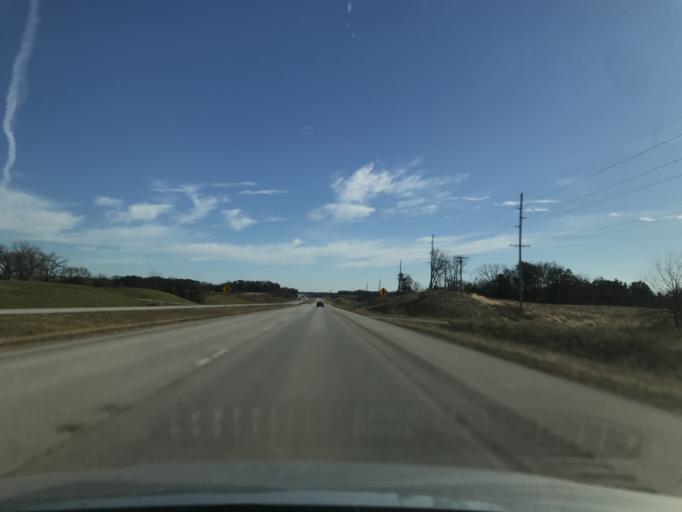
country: US
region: Illinois
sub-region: Hancock County
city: Carthage
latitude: 40.4146
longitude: -91.0387
